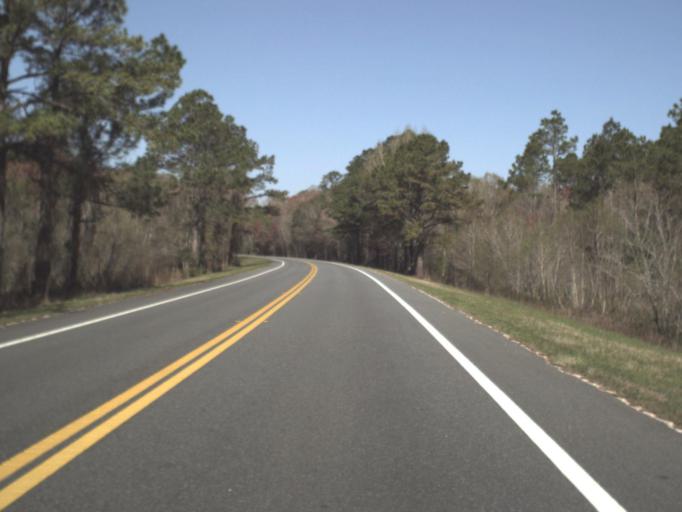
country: US
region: Florida
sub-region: Leon County
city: Woodville
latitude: 30.1844
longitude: -84.0164
